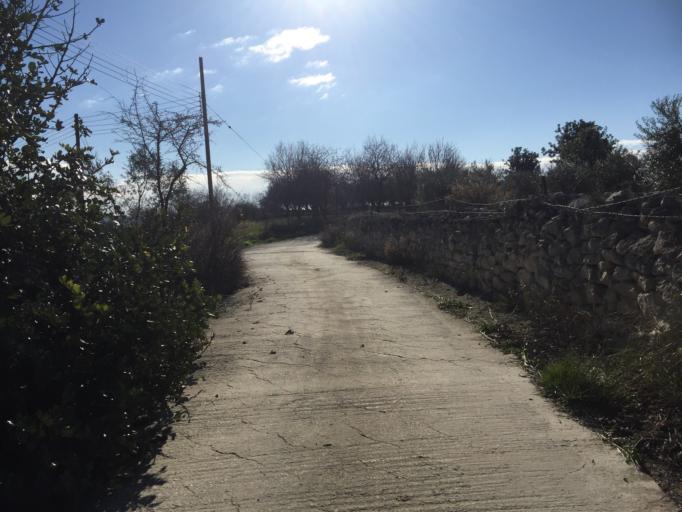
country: CY
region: Pafos
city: Mesogi
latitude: 34.8408
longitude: 32.5093
